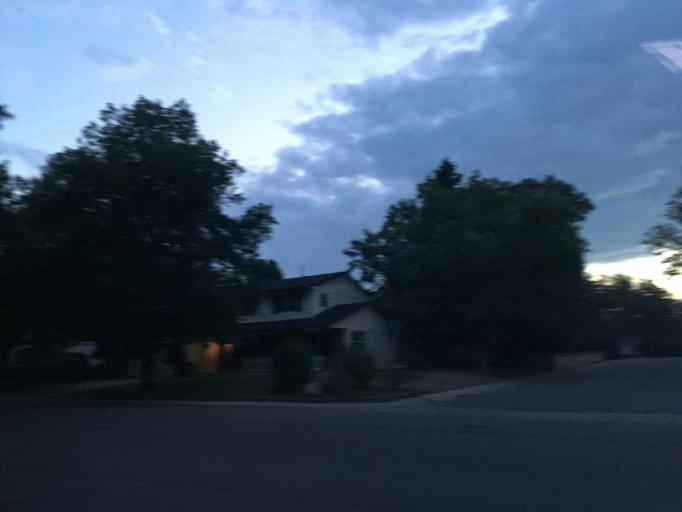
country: US
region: Colorado
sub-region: Adams County
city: Aurora
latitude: 39.6844
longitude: -104.8505
